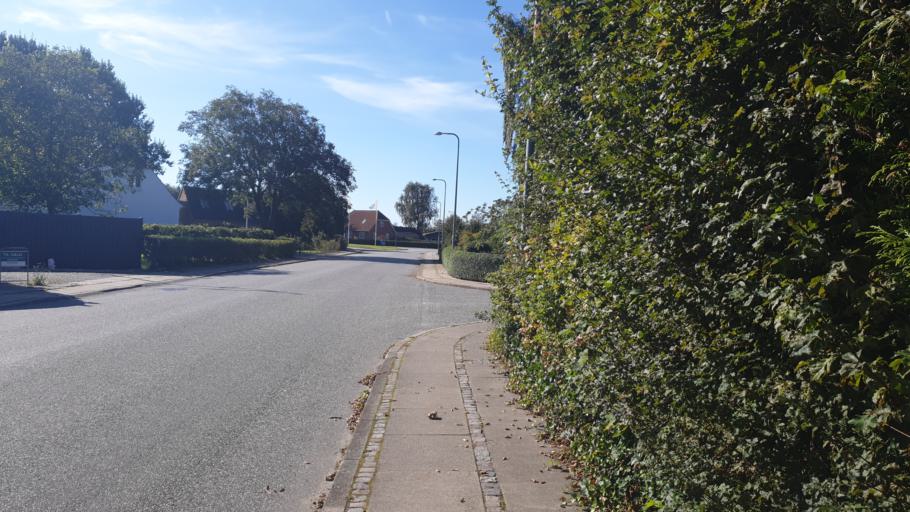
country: DK
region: Central Jutland
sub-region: Hedensted Kommune
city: Hedensted
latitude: 55.7994
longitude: 9.6993
